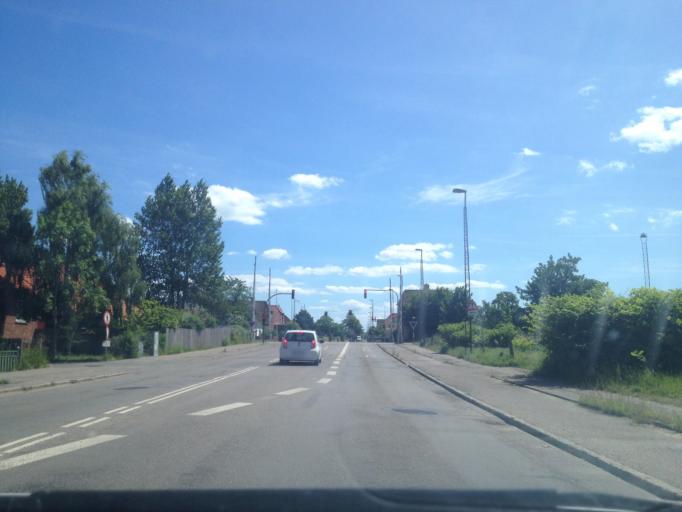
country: DK
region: Zealand
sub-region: Kalundborg Kommune
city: Kalundborg
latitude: 55.6781
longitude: 11.1056
